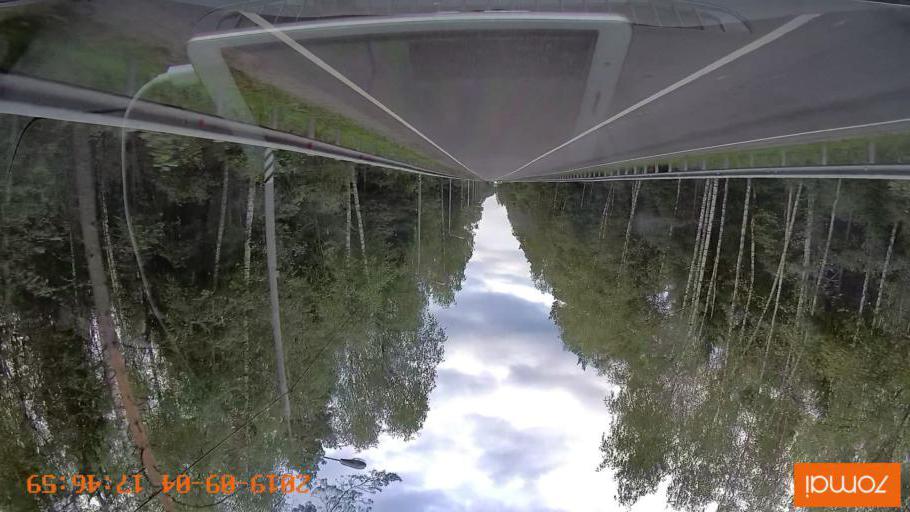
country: RU
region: Moskovskaya
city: Imeni Tsyurupy
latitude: 55.5515
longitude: 38.6305
